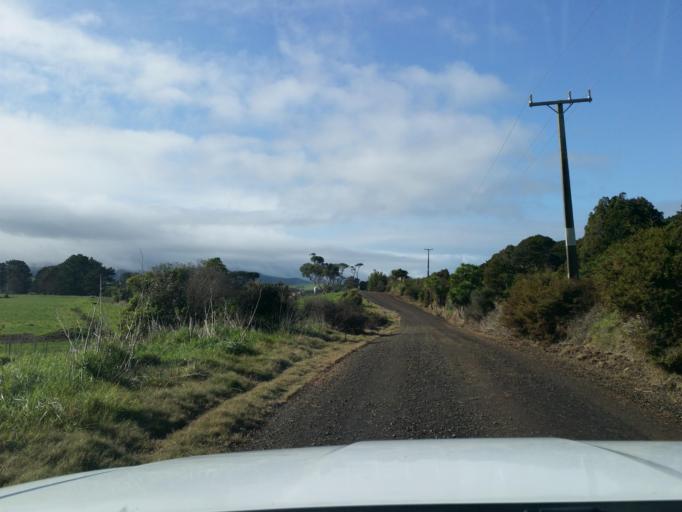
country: NZ
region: Northland
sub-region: Kaipara District
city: Dargaville
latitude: -35.7486
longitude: 173.5811
